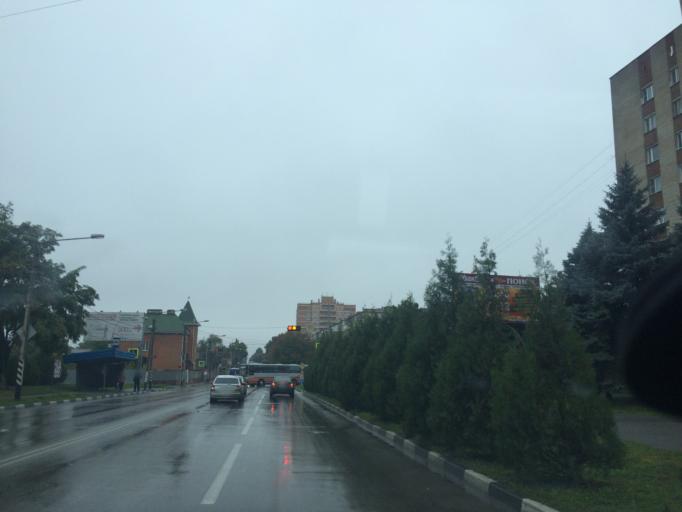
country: RU
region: Rostov
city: Azov
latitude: 47.1067
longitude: 39.4309
